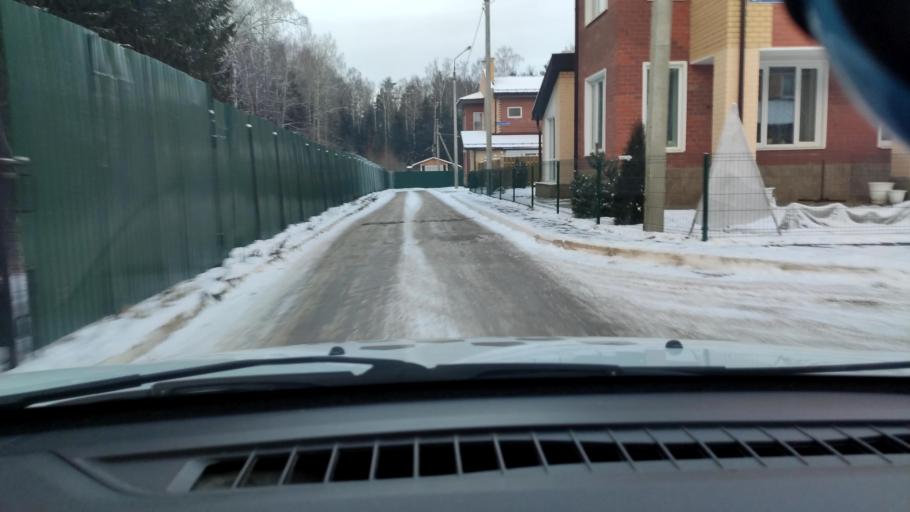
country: RU
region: Perm
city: Kondratovo
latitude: 58.0481
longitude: 56.0823
